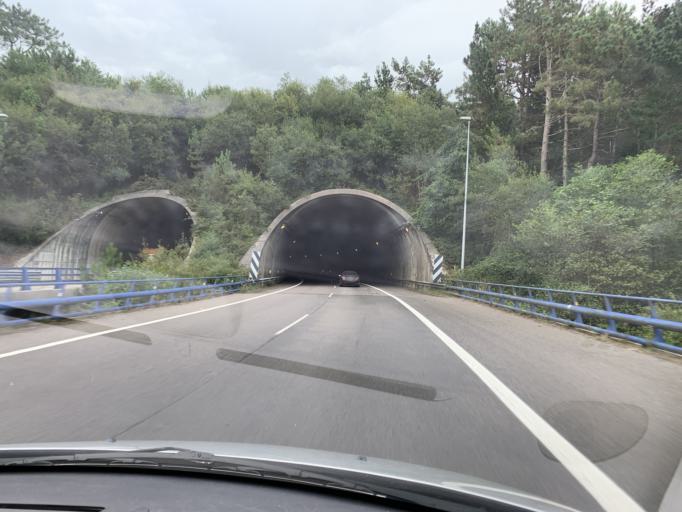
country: ES
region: Asturias
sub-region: Province of Asturias
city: Salas
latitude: 43.5407
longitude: -6.3627
